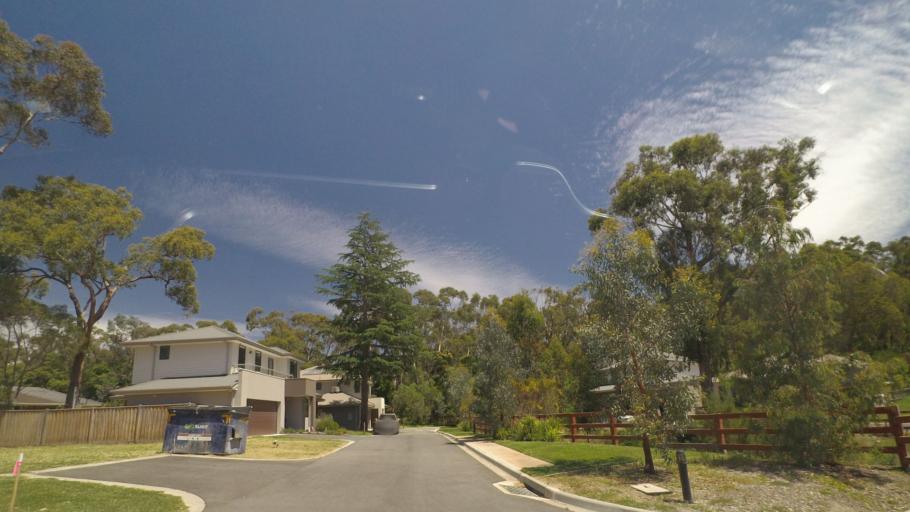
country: AU
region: Victoria
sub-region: Maroondah
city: Croydon North
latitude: -37.7592
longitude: 145.2885
